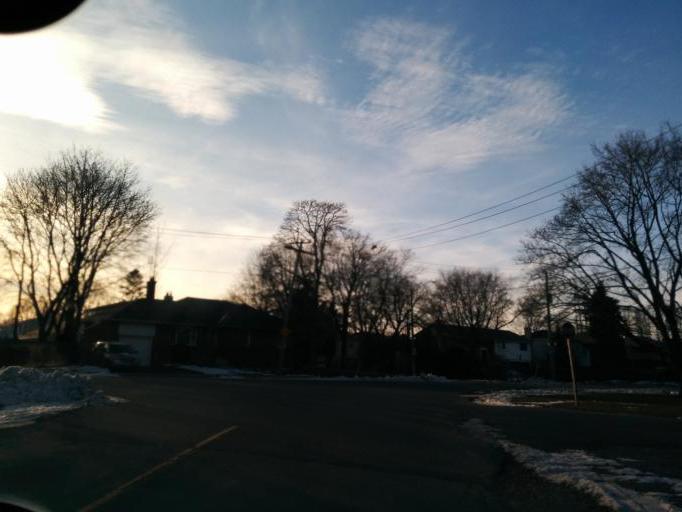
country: CA
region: Ontario
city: Etobicoke
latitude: 43.5933
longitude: -79.5753
